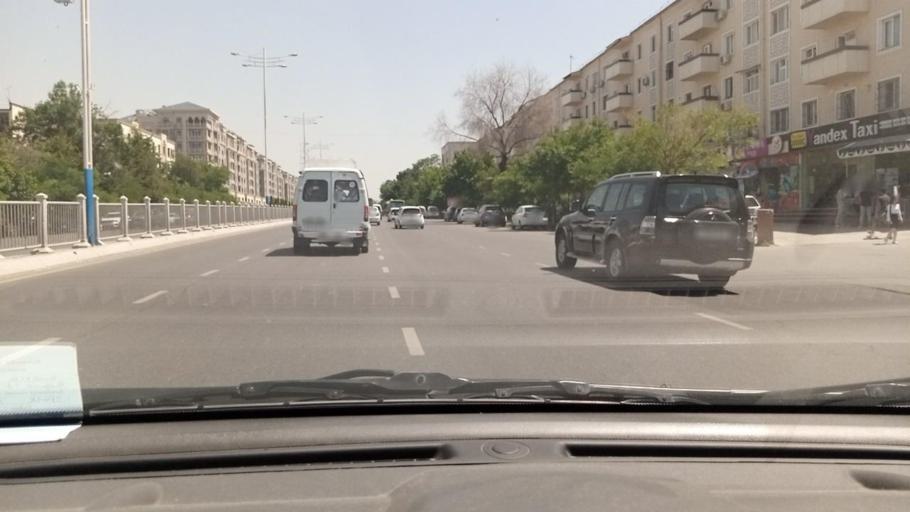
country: UZ
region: Toshkent Shahri
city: Tashkent
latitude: 41.2913
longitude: 69.2240
